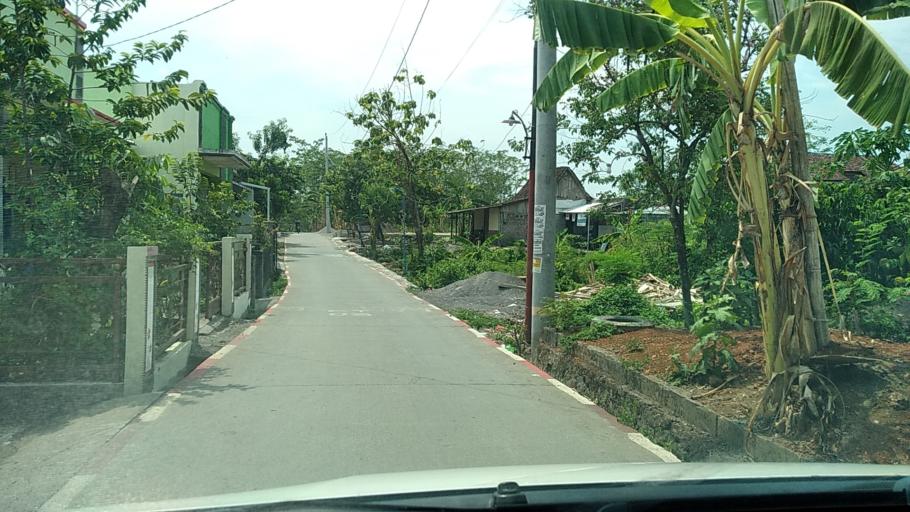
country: ID
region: Central Java
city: Mranggen
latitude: -7.0555
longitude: 110.4731
